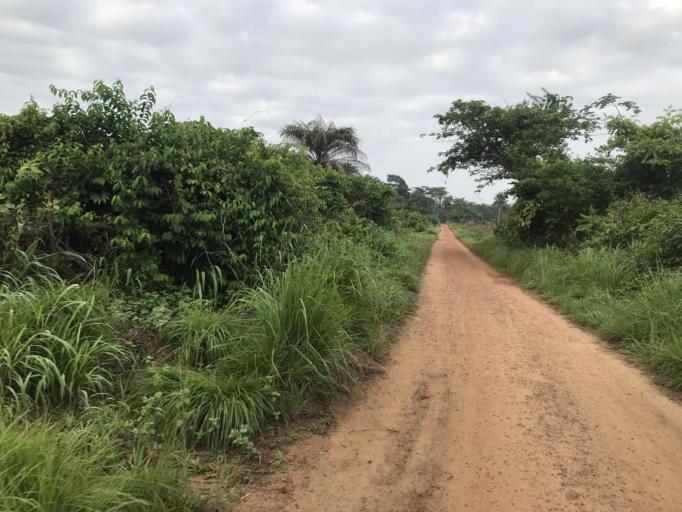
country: SL
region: Eastern Province
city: Pendembu
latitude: 8.0886
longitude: -10.6961
